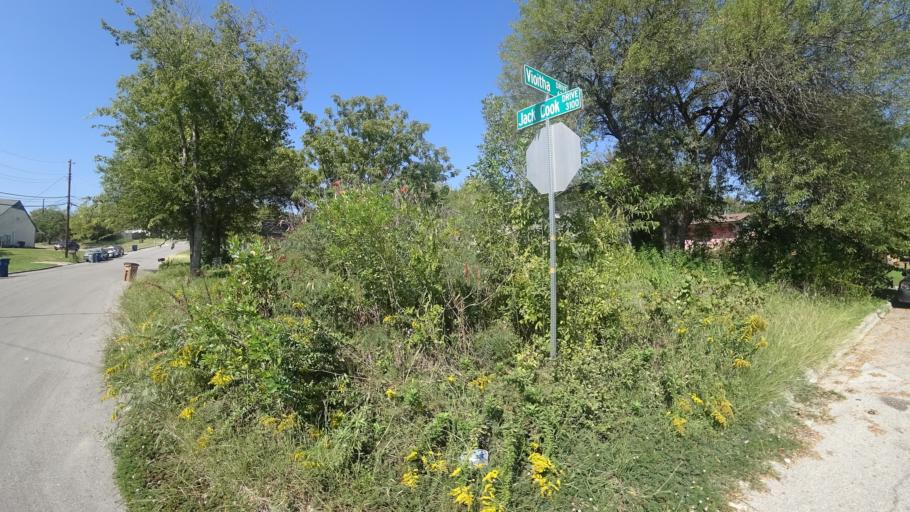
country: US
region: Texas
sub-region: Travis County
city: Austin
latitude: 30.3087
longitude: -97.6727
